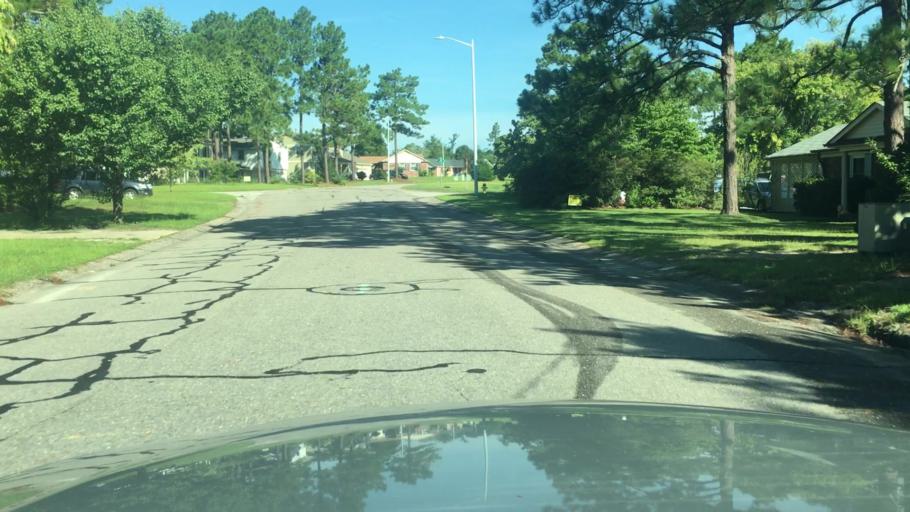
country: US
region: North Carolina
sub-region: Cumberland County
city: Spring Lake
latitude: 35.1422
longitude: -78.9014
